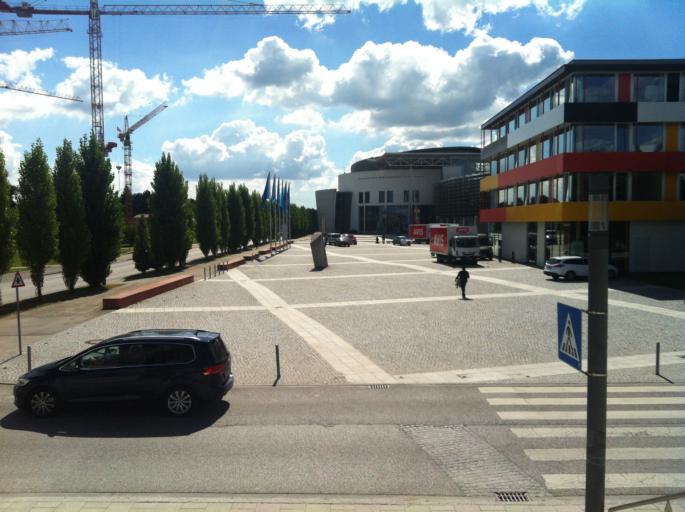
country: DE
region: Bavaria
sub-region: Upper Bavaria
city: Garching bei Munchen
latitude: 48.2669
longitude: 11.6715
